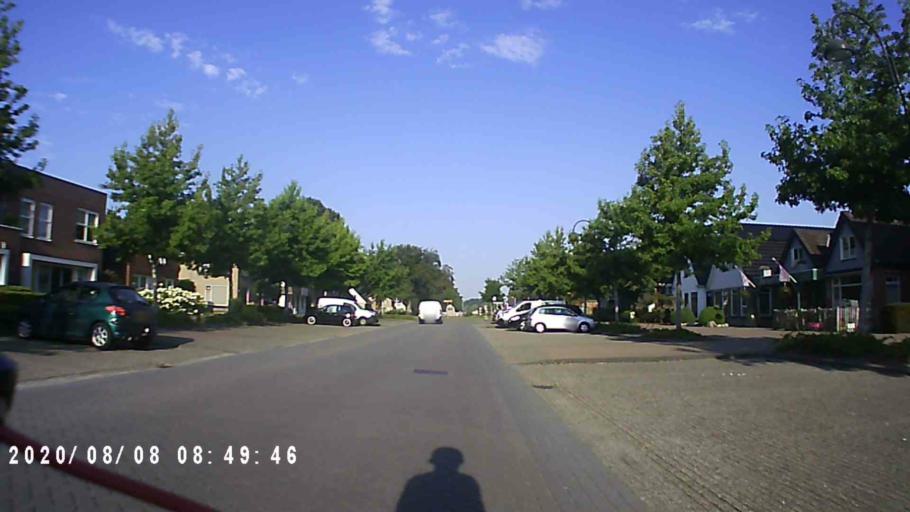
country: NL
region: Groningen
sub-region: Gemeente Leek
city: Leek
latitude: 53.0655
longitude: 6.3309
